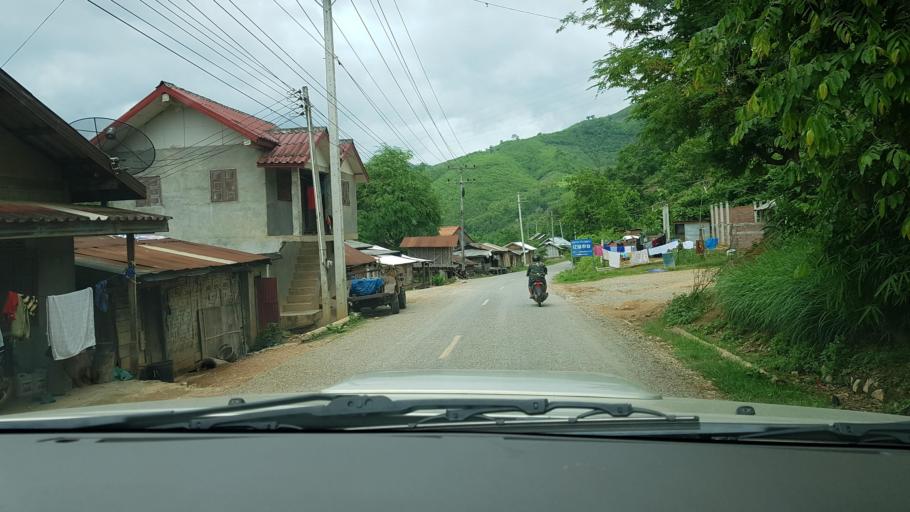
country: TH
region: Nan
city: Chaloem Phra Kiat
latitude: 19.9622
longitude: 101.2628
